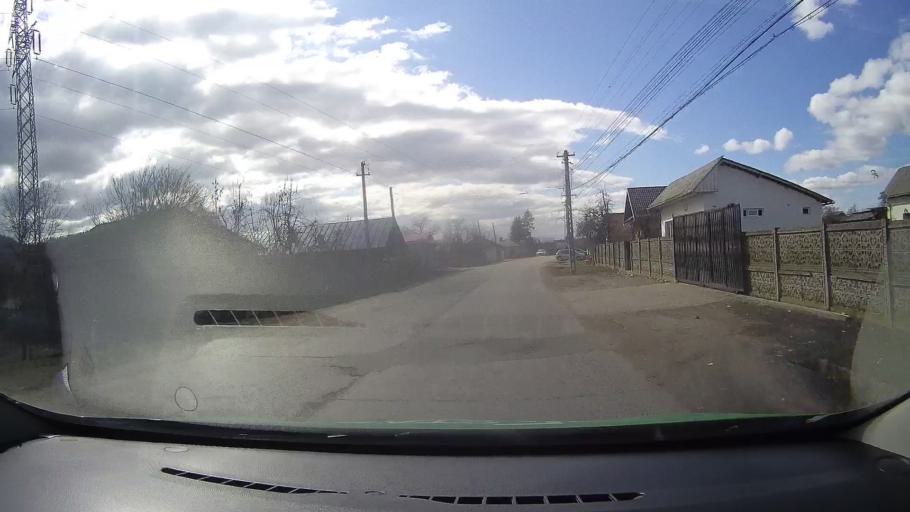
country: RO
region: Dambovita
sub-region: Comuna Branesti
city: Branesti
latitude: 45.0287
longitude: 25.4096
